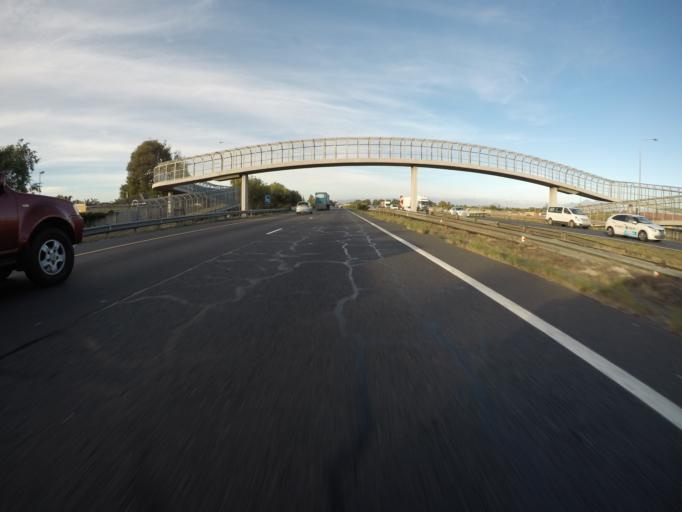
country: ZA
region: Western Cape
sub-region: City of Cape Town
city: Kraaifontein
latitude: -33.8490
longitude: 18.7092
